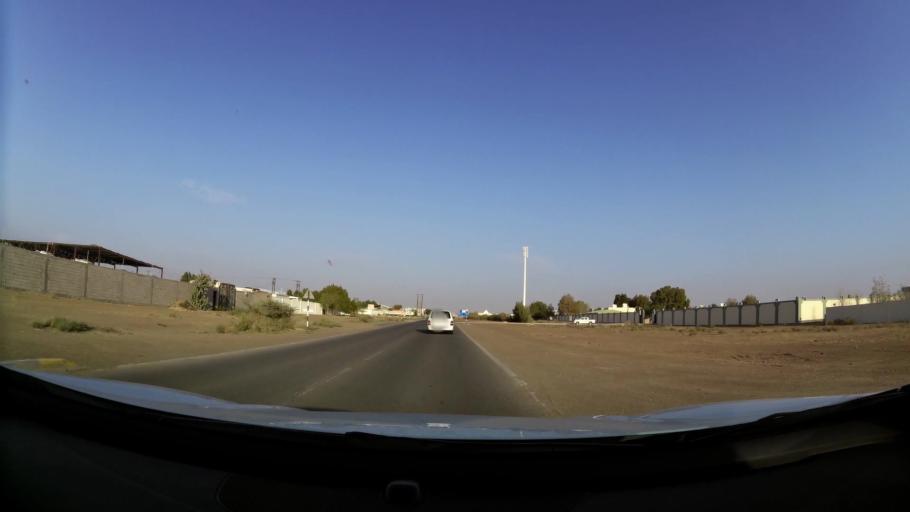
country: AE
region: Abu Dhabi
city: Al Ain
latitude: 24.1410
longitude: 55.8316
